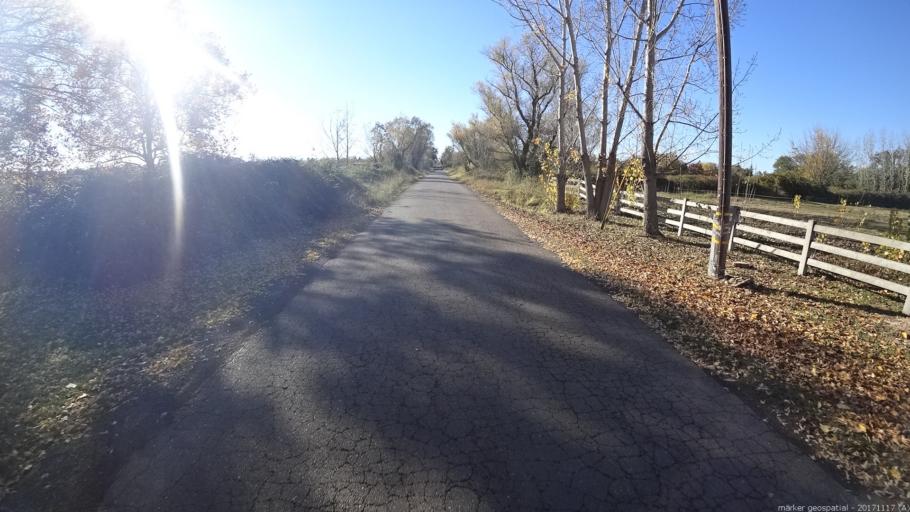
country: US
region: California
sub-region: Shasta County
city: Cottonwood
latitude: 40.4033
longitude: -122.2217
